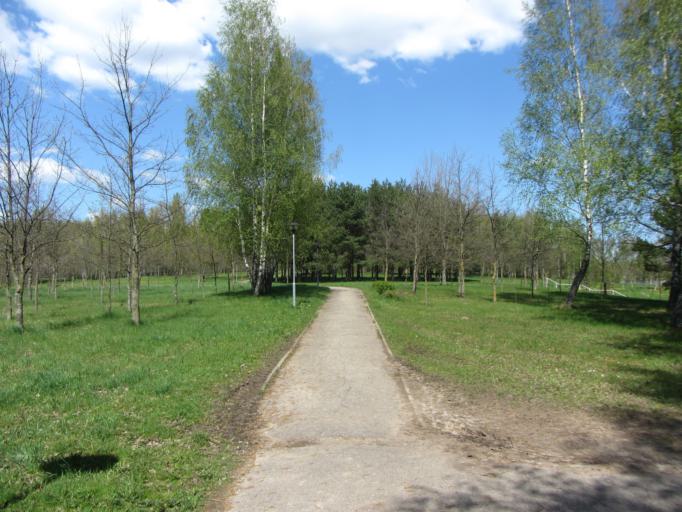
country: LT
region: Vilnius County
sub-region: Vilnius
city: Fabijoniskes
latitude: 54.7526
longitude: 25.2747
